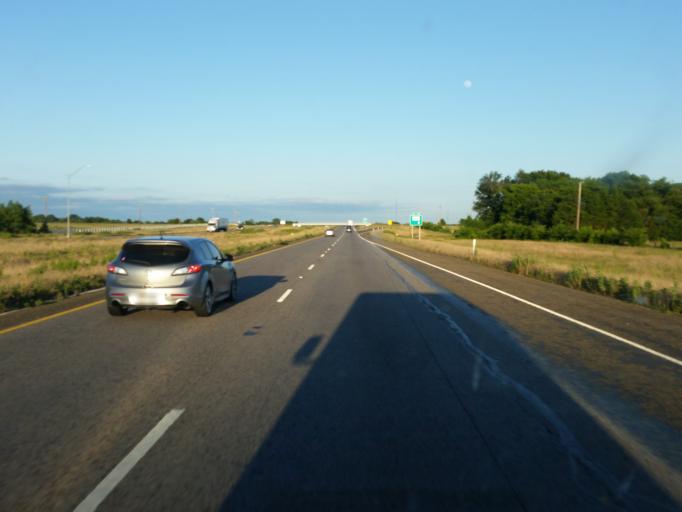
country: US
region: Texas
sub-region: Van Zandt County
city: Wills Point
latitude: 32.6575
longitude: -96.1029
